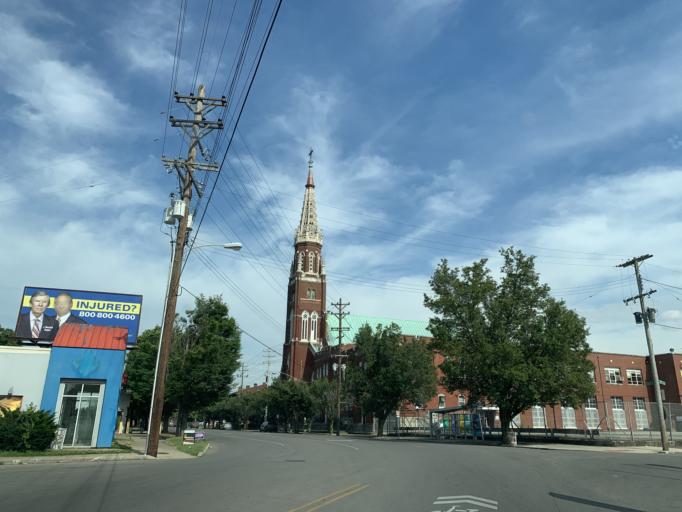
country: US
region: Kentucky
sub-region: Jefferson County
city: Louisville
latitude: 38.2590
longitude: -85.7891
